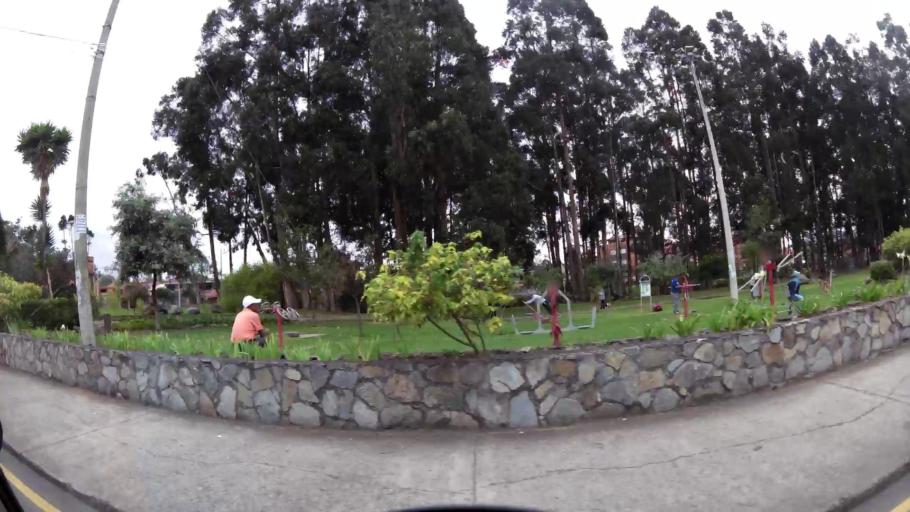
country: EC
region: Azuay
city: Cuenca
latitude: -2.9133
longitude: -79.0129
